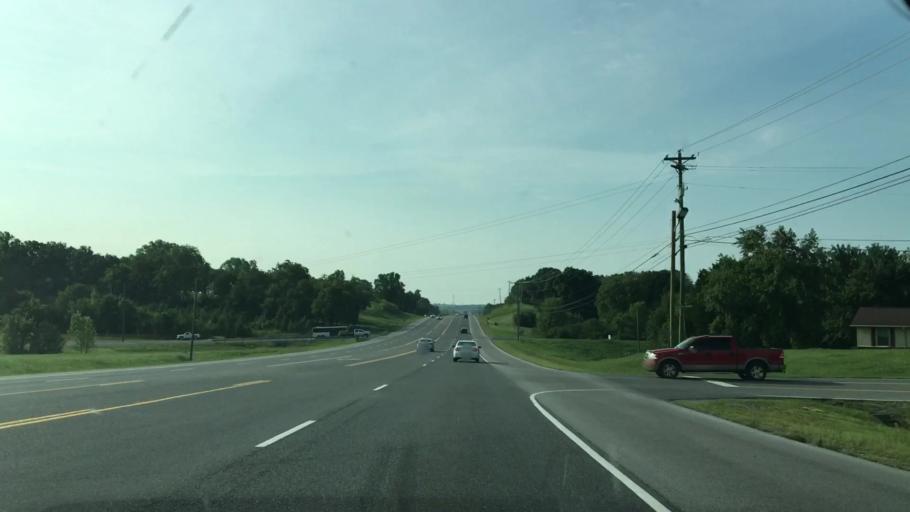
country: US
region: Tennessee
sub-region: Wilson County
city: Mount Juliet
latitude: 36.2033
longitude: -86.4172
